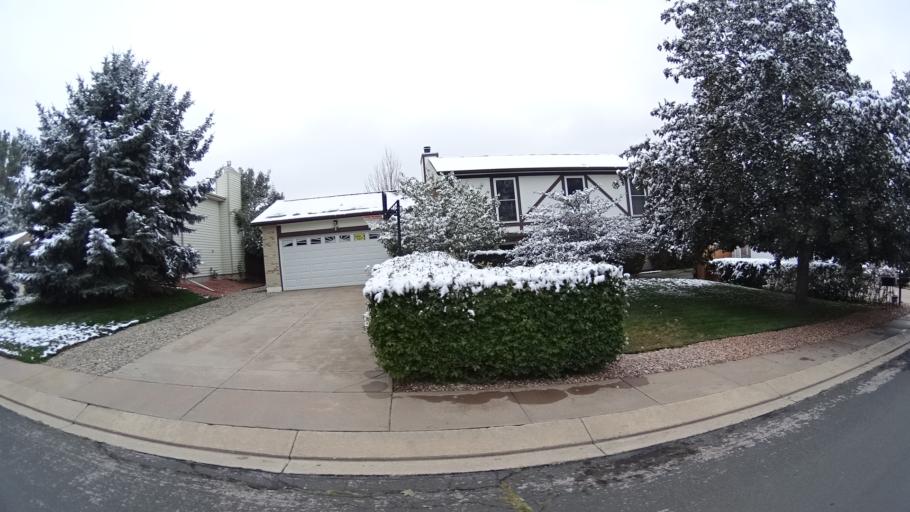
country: US
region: Colorado
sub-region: El Paso County
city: Cimarron Hills
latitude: 38.9286
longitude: -104.7668
